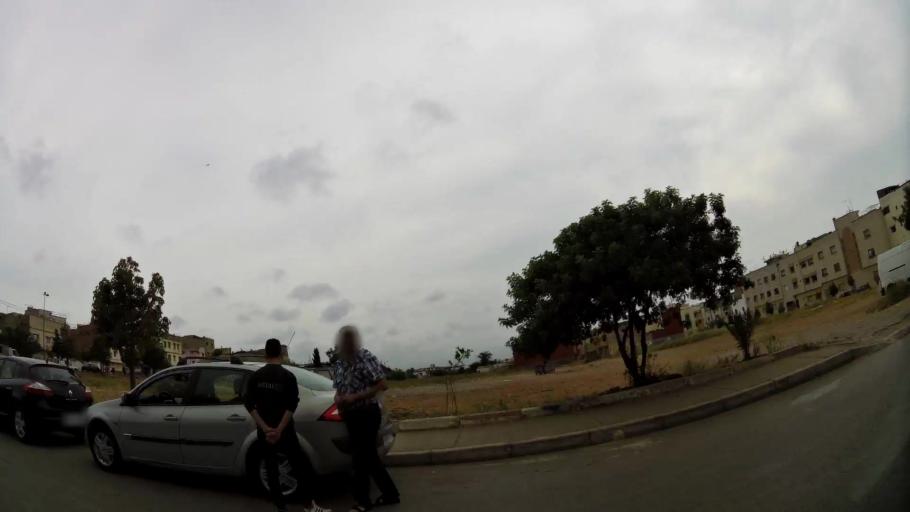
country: MA
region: Rabat-Sale-Zemmour-Zaer
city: Sale
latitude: 34.0308
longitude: -6.8054
